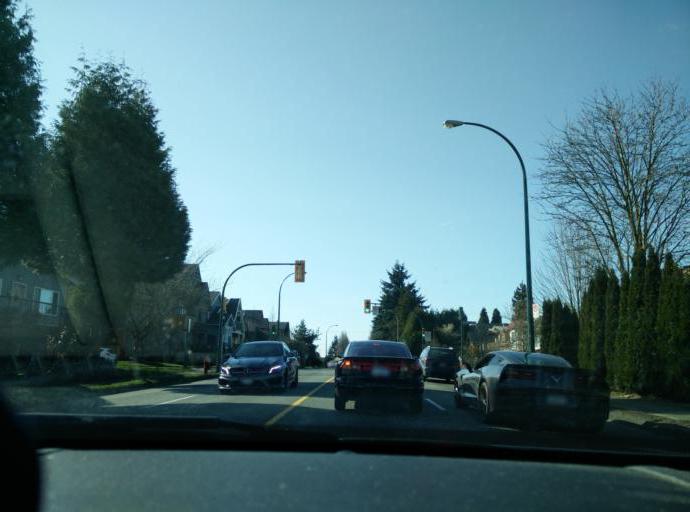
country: CA
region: British Columbia
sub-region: Fraser Valley Regional District
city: North Vancouver
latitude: 49.2696
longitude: -123.0594
